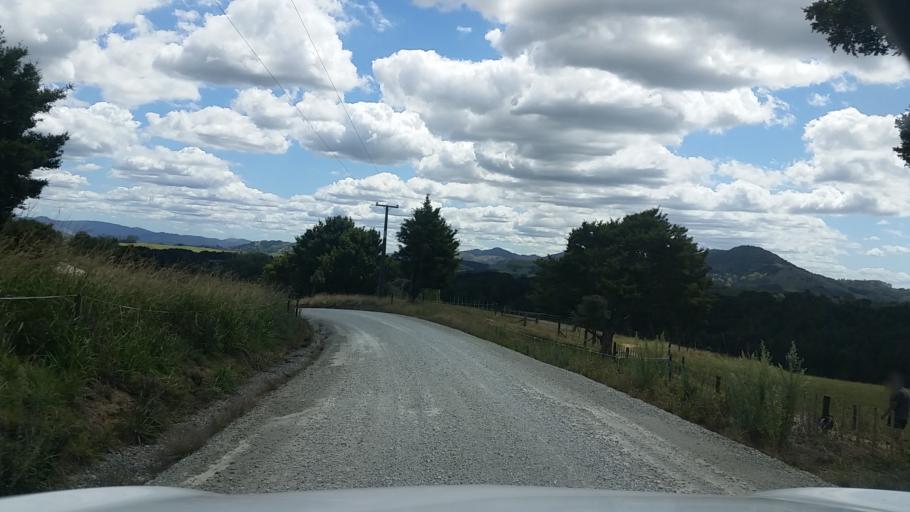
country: NZ
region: Northland
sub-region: Whangarei
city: Maungatapere
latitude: -35.6681
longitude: 174.1694
